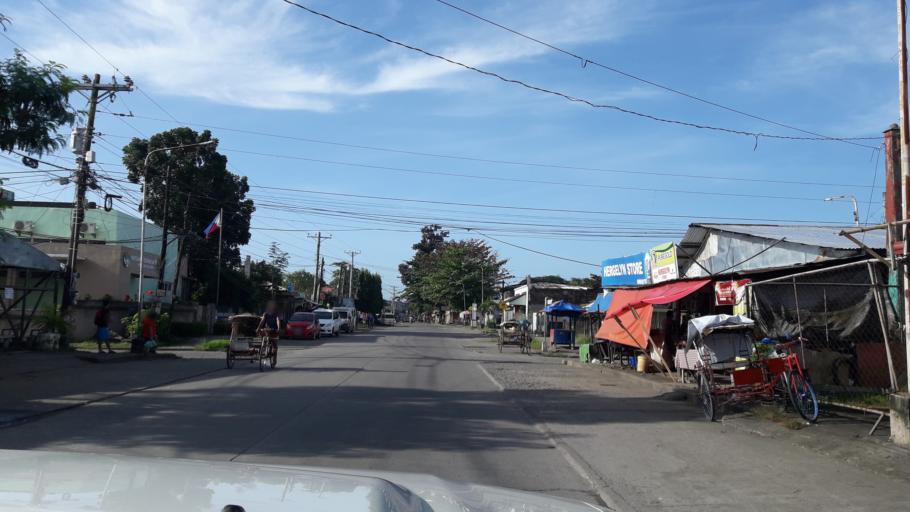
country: PH
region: Eastern Visayas
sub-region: Province of Leyte
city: Panalanoy
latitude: 11.2174
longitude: 125.0024
